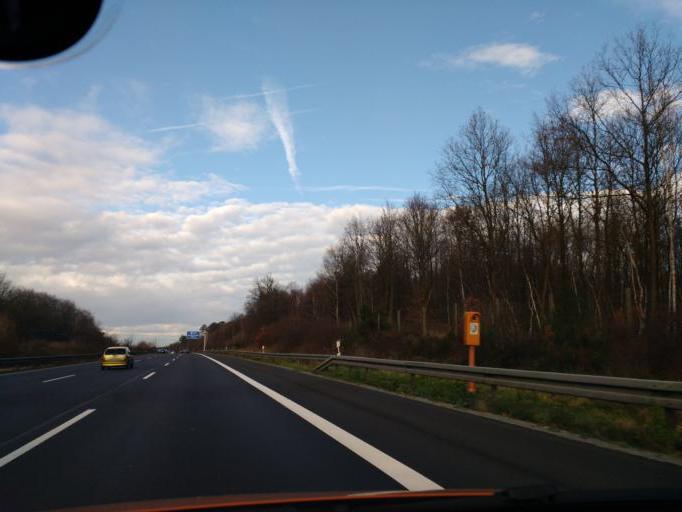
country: DE
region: Lower Saxony
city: Mariental
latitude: 52.2537
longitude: 10.9975
